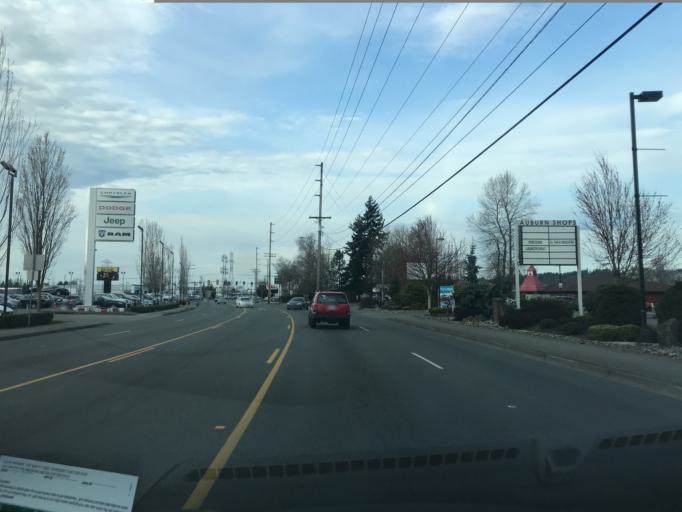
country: US
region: Washington
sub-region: King County
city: Auburn
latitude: 47.3323
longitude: -122.2216
